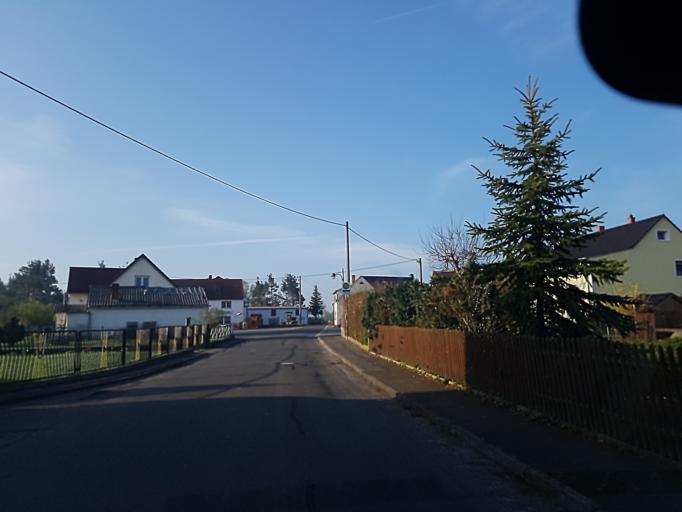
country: DE
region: Saxony
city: Cavertitz
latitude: 51.4241
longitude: 13.1541
